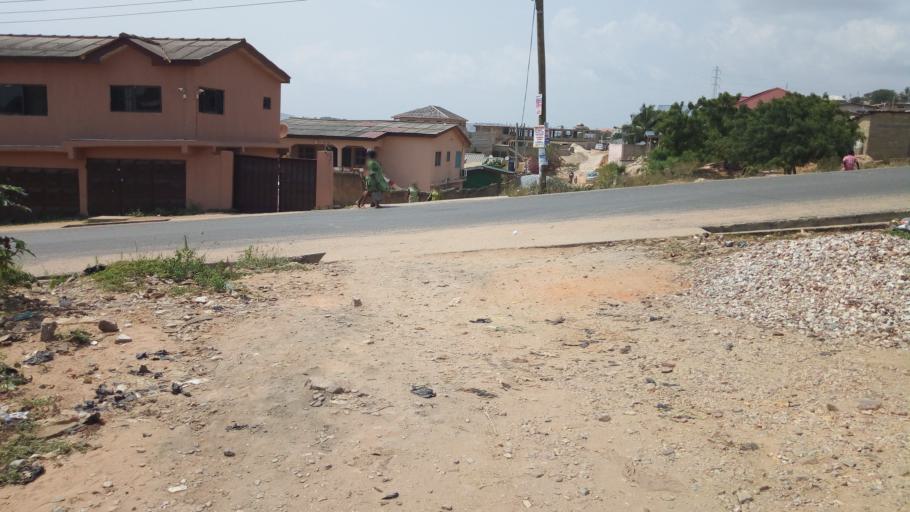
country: GH
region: Greater Accra
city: Gbawe
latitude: 5.5625
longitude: -0.3098
